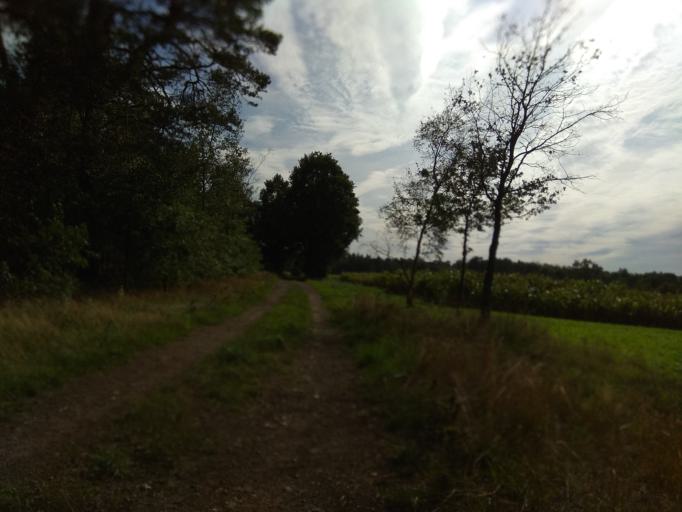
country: DE
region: North Rhine-Westphalia
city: Marl
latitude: 51.7125
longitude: 7.0426
